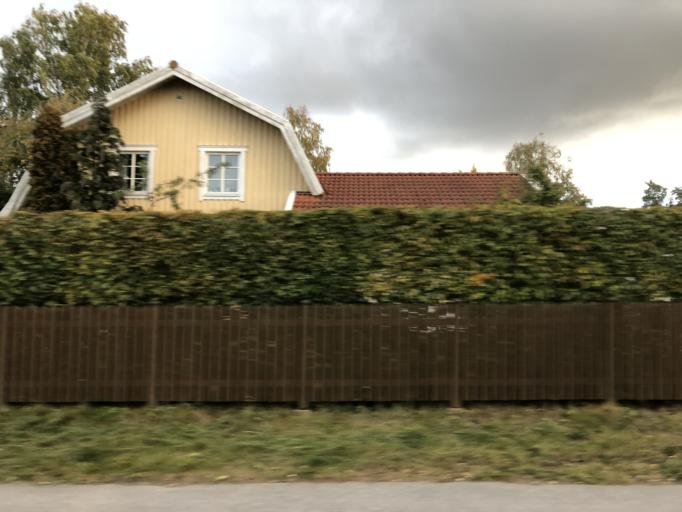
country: SE
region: Stockholm
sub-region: Jarfalla Kommun
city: Jakobsberg
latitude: 59.4281
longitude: 17.8133
